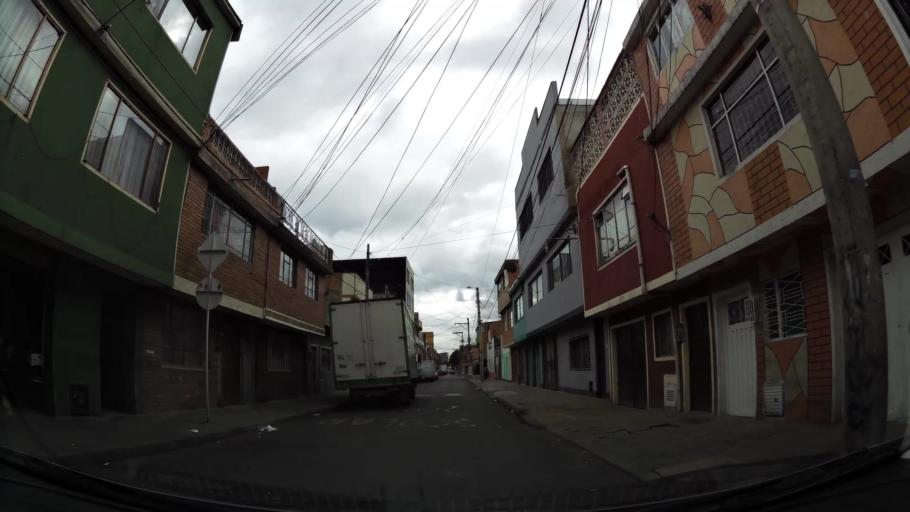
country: CO
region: Bogota D.C.
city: Barrio San Luis
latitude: 4.7067
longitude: -74.1048
